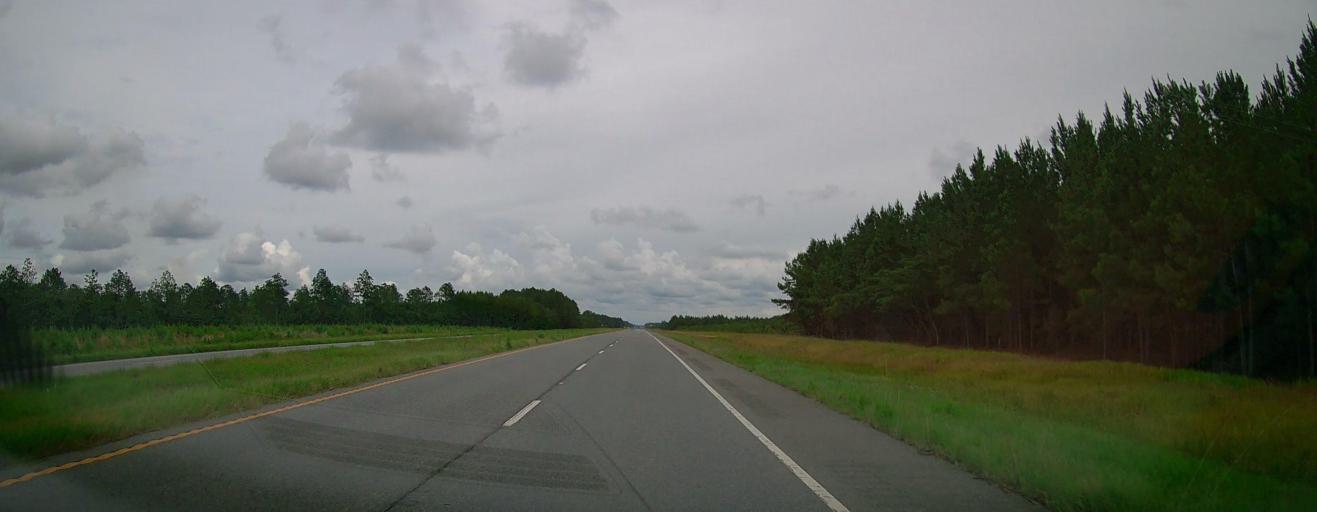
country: US
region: Georgia
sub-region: Appling County
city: Baxley
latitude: 31.7546
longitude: -82.2798
